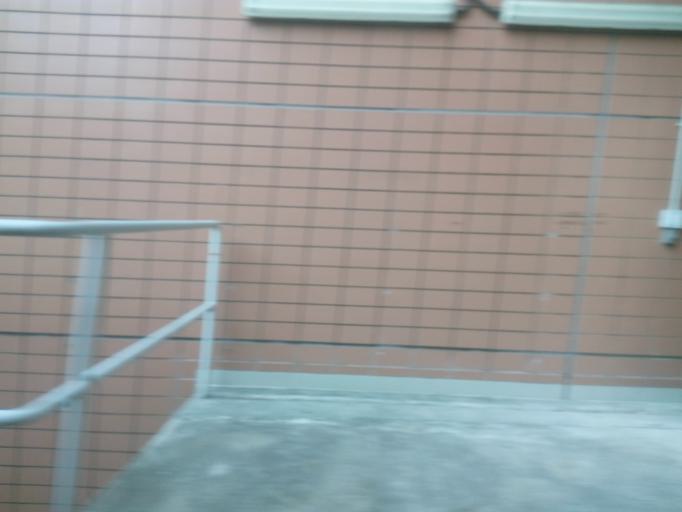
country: HK
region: Sai Kung
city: Sai Kung
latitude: 22.4289
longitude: 114.2429
